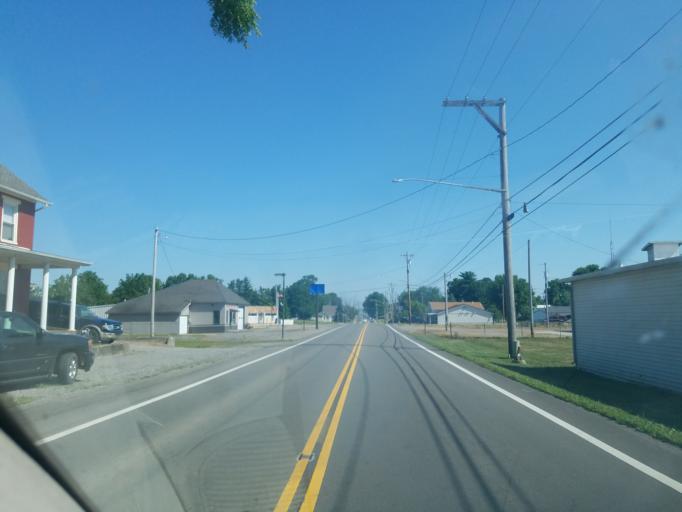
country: US
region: Ohio
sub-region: Logan County
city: Northwood
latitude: 40.4396
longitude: -83.8053
